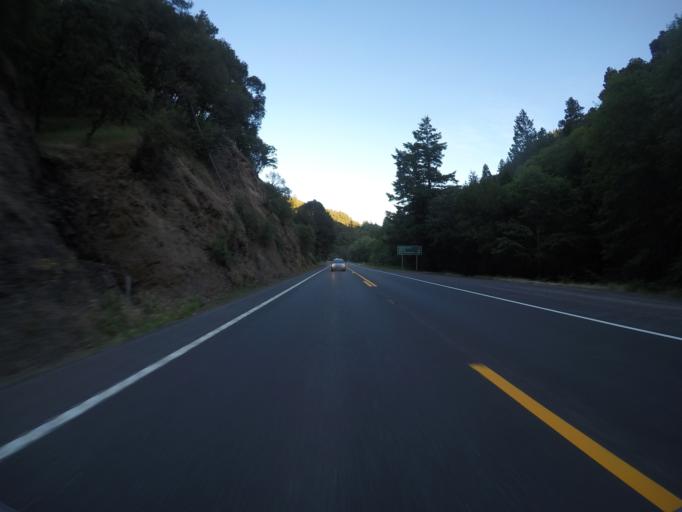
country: US
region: California
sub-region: Mendocino County
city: Laytonville
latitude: 39.8241
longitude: -123.5668
